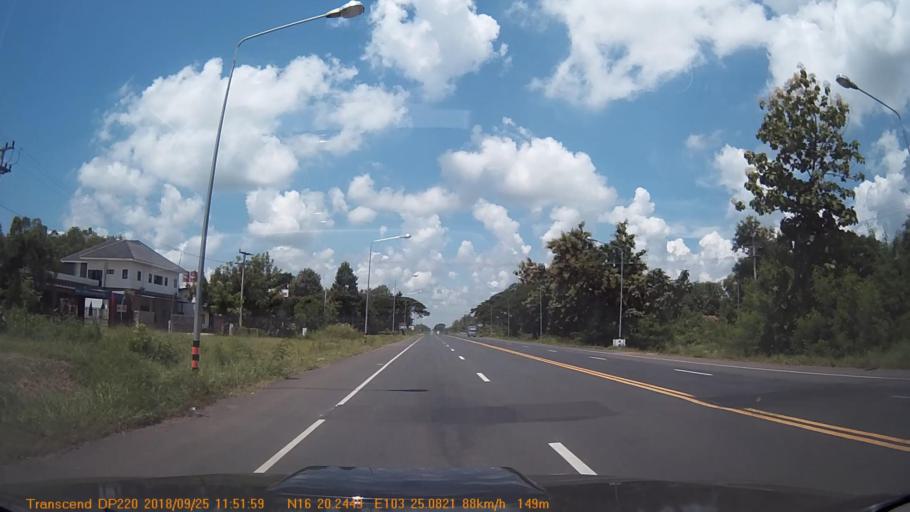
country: TH
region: Kalasin
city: Yang Talat
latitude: 16.3375
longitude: 103.4180
